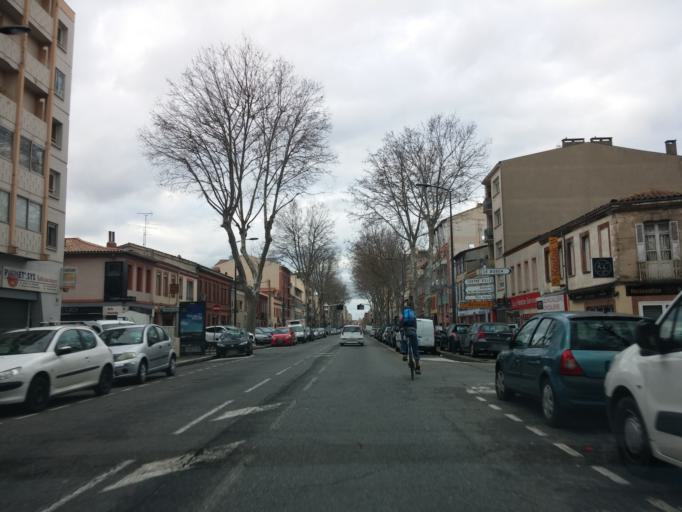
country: FR
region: Midi-Pyrenees
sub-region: Departement de la Haute-Garonne
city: Toulouse
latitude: 43.5814
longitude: 1.4490
